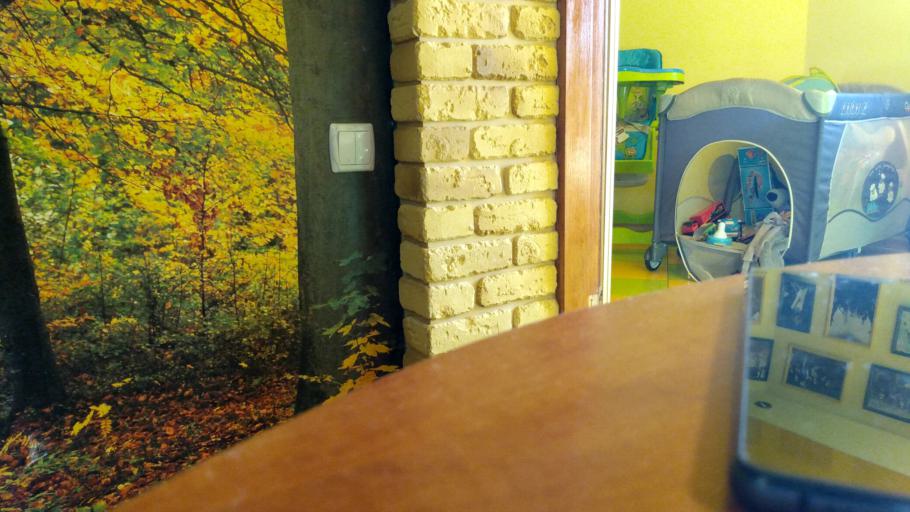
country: RU
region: Tverskaya
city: Likhoslavl'
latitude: 57.1814
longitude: 35.5521
